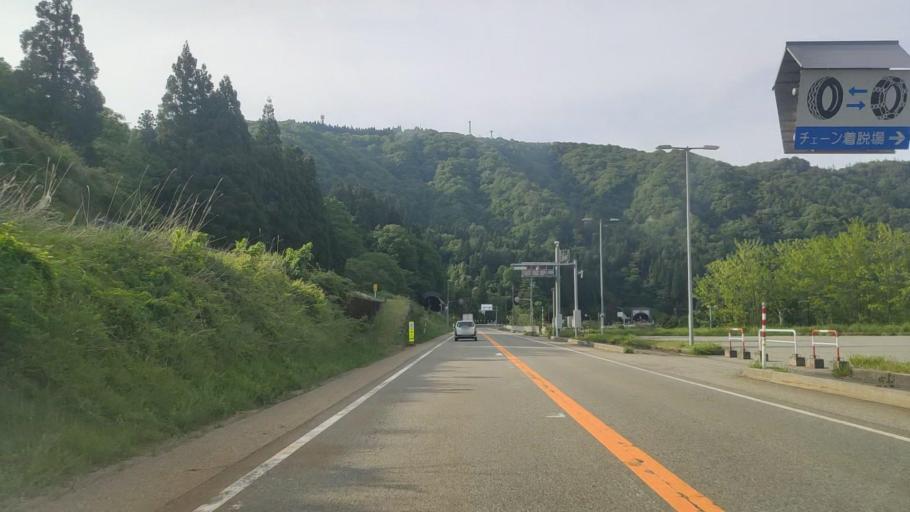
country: JP
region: Toyama
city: Yatsuomachi-higashikumisaka
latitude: 36.4922
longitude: 137.2365
